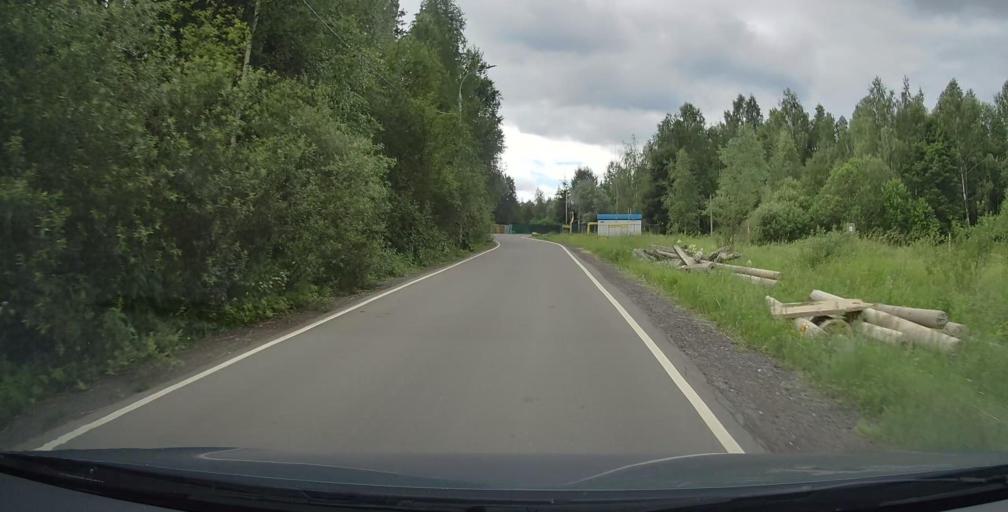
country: RU
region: Moskovskaya
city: Selyatino
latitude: 55.3968
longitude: 37.0097
